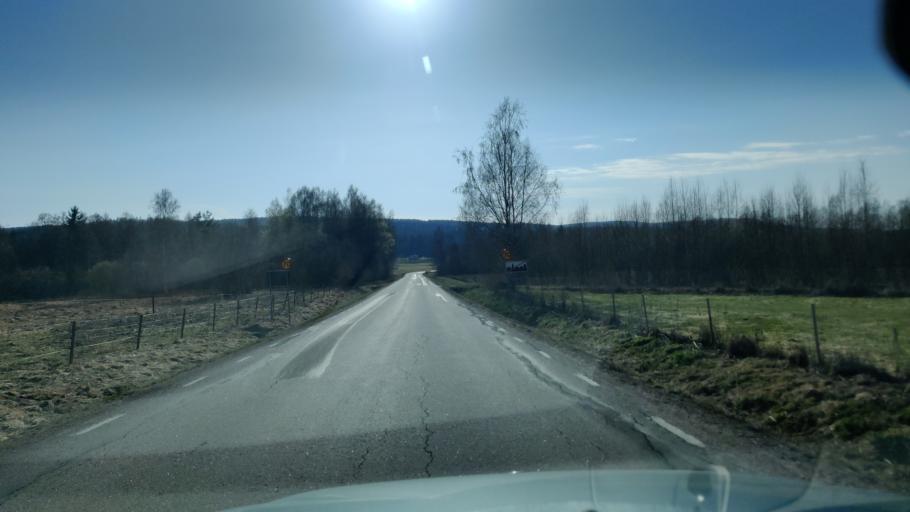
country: SE
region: Vaermland
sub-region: Munkfors Kommun
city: Munkfors
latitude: 59.9675
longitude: 13.4829
